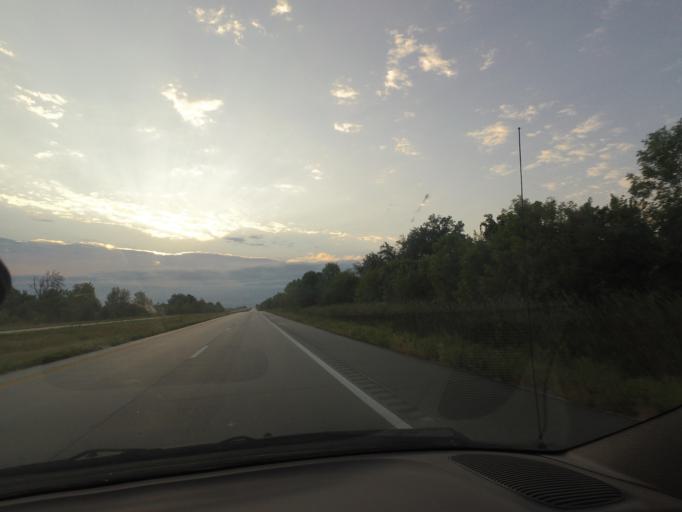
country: US
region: Missouri
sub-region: Shelby County
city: Shelbina
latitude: 39.7330
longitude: -92.2084
